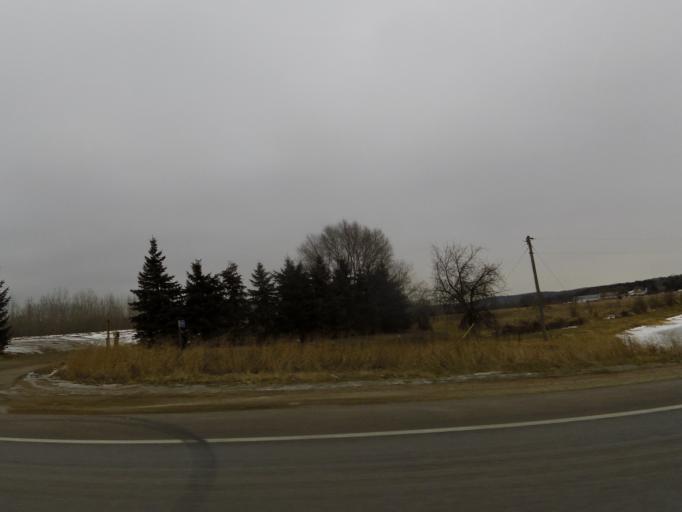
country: US
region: Minnesota
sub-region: Scott County
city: Jordan
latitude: 44.6900
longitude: -93.6412
